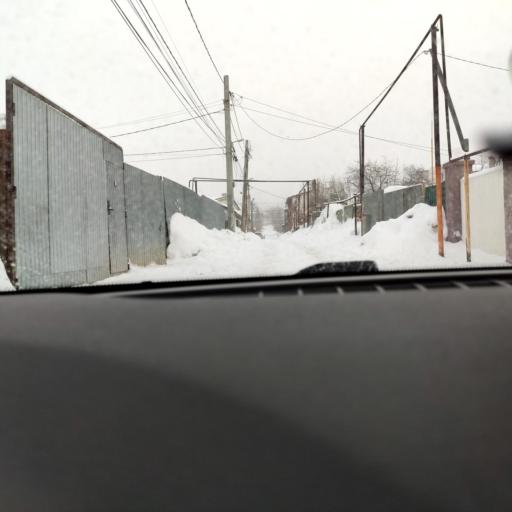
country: RU
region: Samara
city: Samara
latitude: 53.2655
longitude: 50.2030
